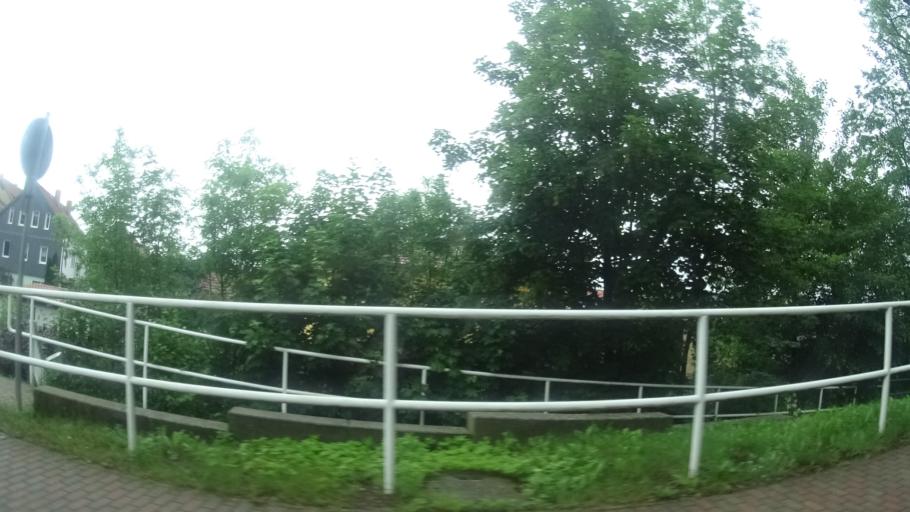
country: DE
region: Thuringia
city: Langewiesen
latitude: 50.6701
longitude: 10.9753
